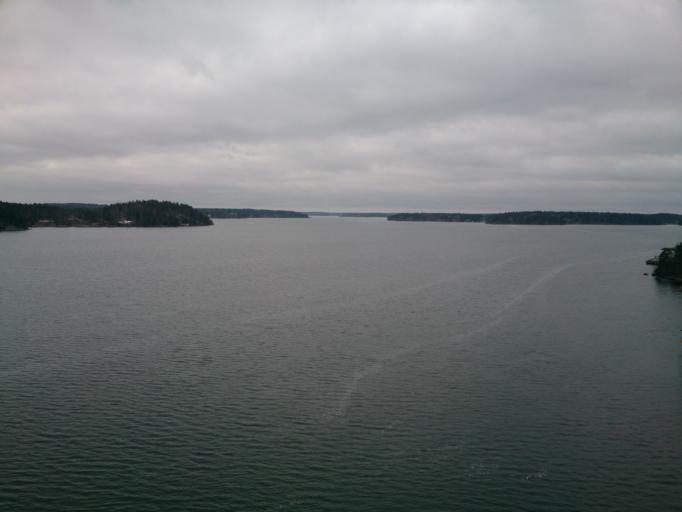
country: SE
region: Stockholm
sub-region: Varmdo Kommun
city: Mortnas
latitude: 59.3963
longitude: 18.4428
